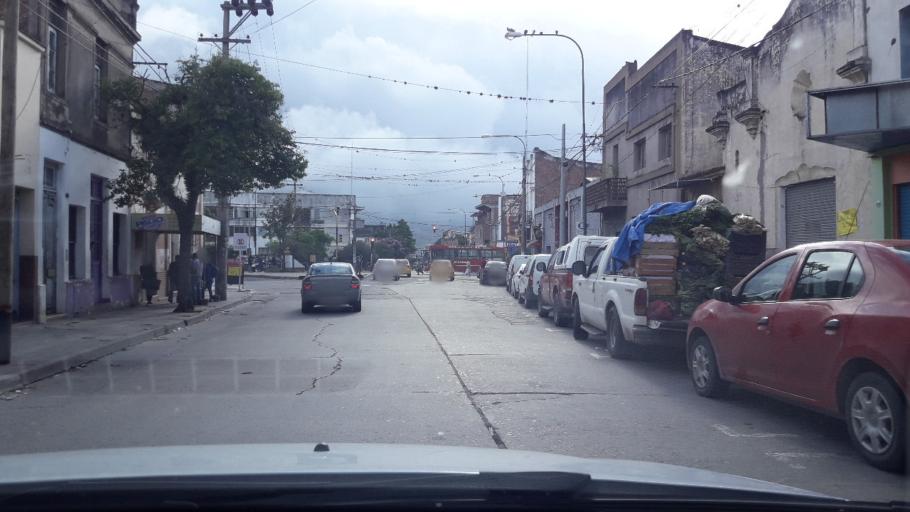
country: AR
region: Jujuy
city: San Salvador de Jujuy
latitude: -24.1909
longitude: -65.3033
